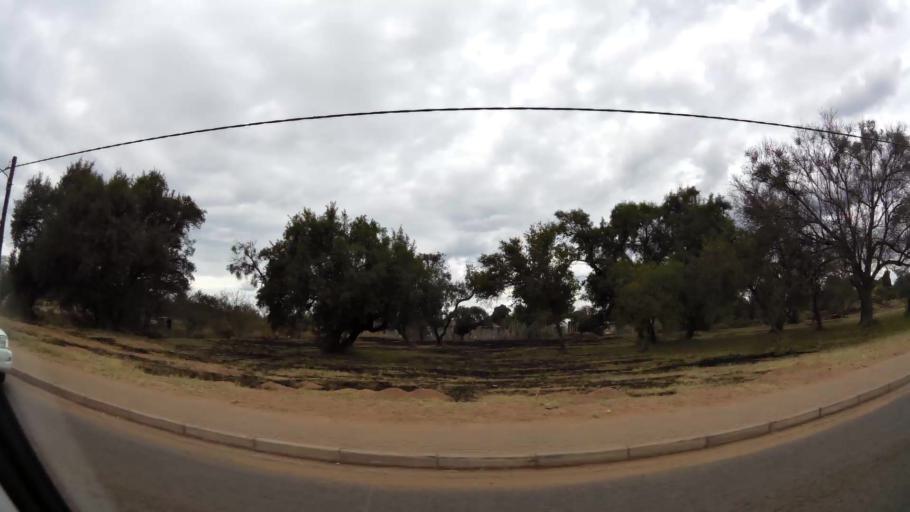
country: ZA
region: Limpopo
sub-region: Waterberg District Municipality
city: Modimolle
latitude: -24.7013
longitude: 28.4146
